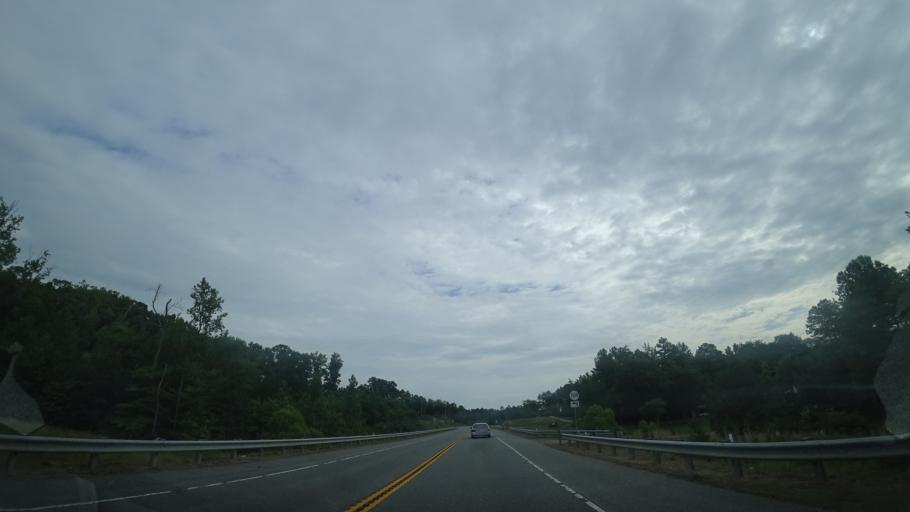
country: US
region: Virginia
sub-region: Spotsylvania County
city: Spotsylvania Courthouse
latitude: 38.1710
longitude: -77.6347
